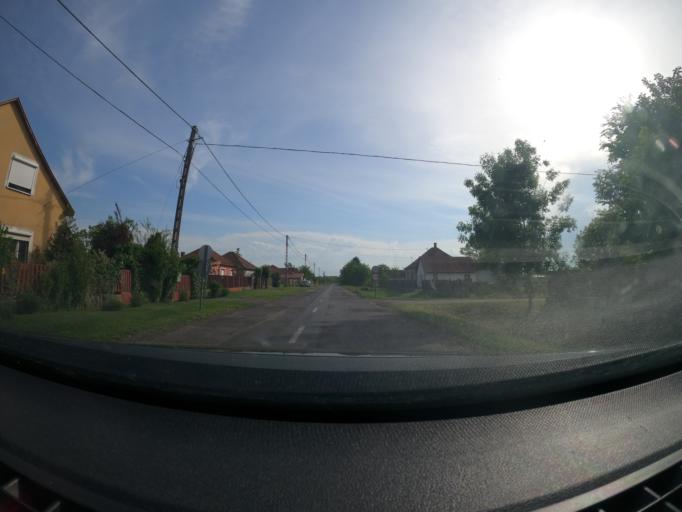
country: HU
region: Hajdu-Bihar
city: Nyirabrany
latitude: 47.5419
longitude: 22.0114
